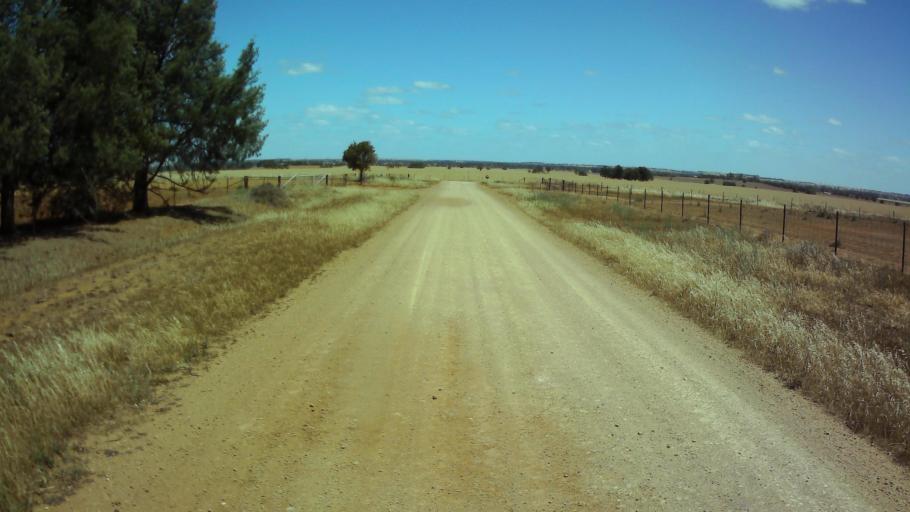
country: AU
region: New South Wales
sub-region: Weddin
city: Grenfell
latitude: -33.9778
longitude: 148.3268
